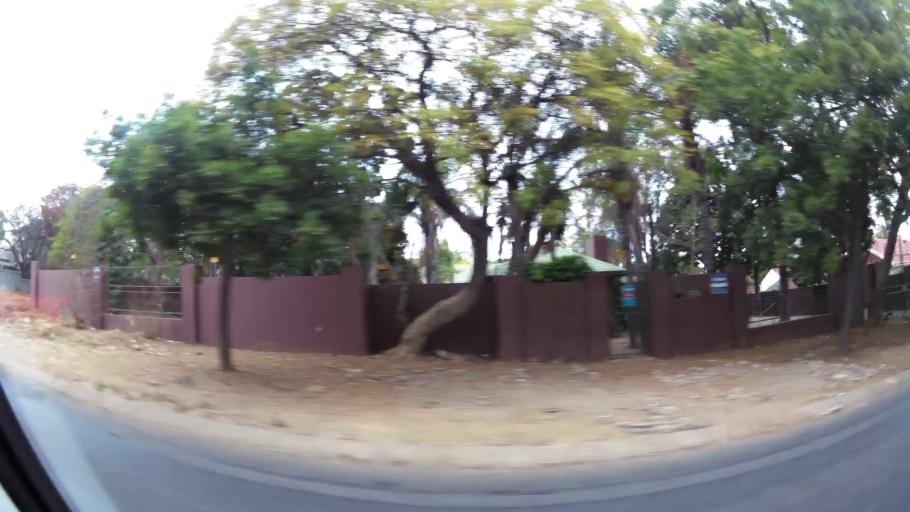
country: ZA
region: Limpopo
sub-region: Capricorn District Municipality
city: Polokwane
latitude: -23.8996
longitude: 29.4662
